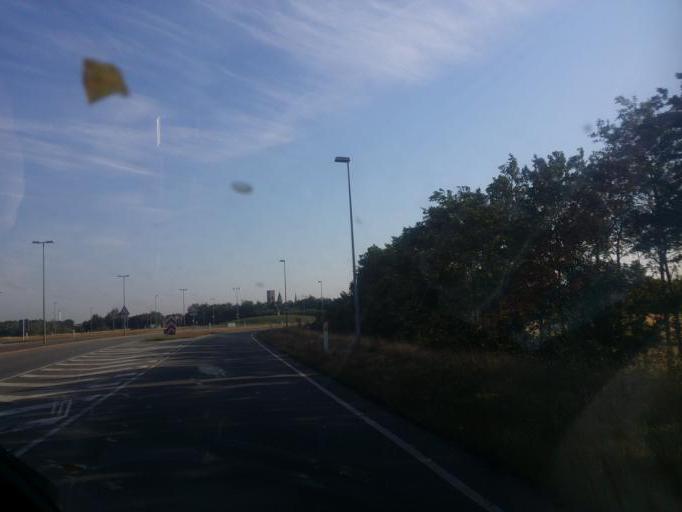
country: DK
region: South Denmark
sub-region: Esbjerg Kommune
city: Ribe
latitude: 55.3197
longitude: 8.7537
